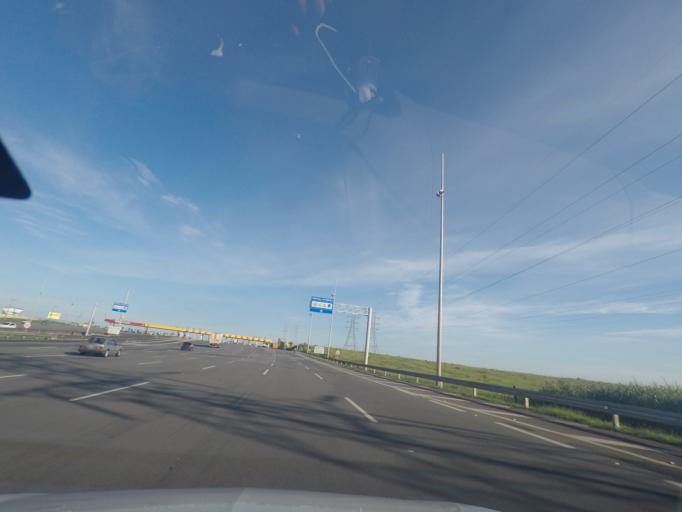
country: BR
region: Sao Paulo
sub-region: Sumare
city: Sumare
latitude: -22.7727
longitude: -47.2363
